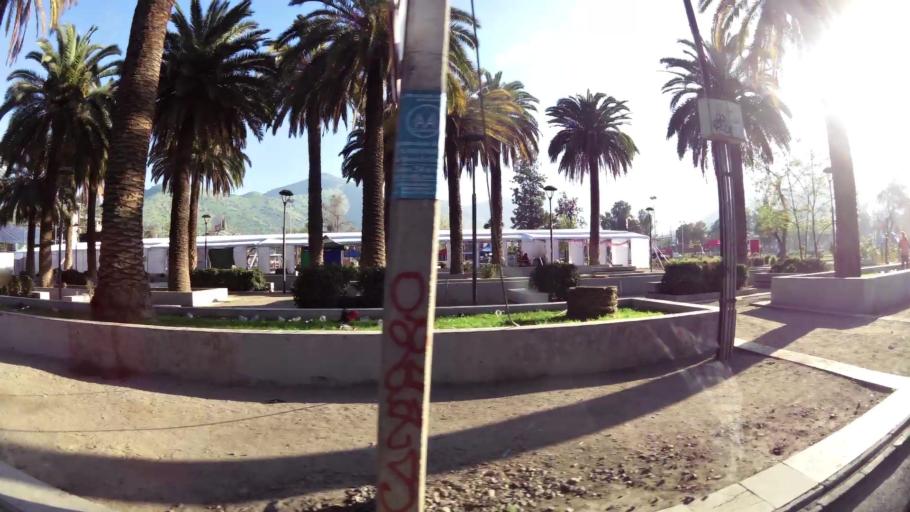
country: CL
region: Santiago Metropolitan
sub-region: Provincia de Santiago
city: Santiago
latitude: -33.3749
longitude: -70.6361
